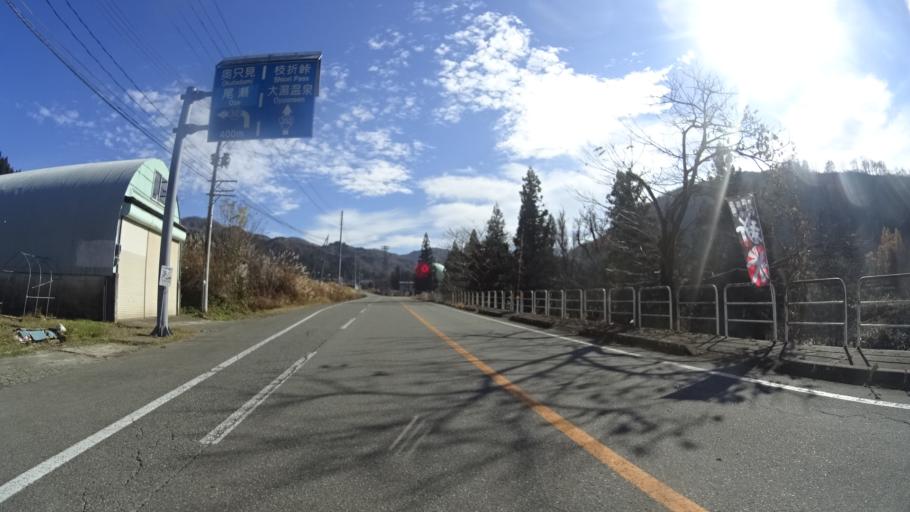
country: JP
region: Niigata
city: Muikamachi
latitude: 37.2067
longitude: 139.0665
